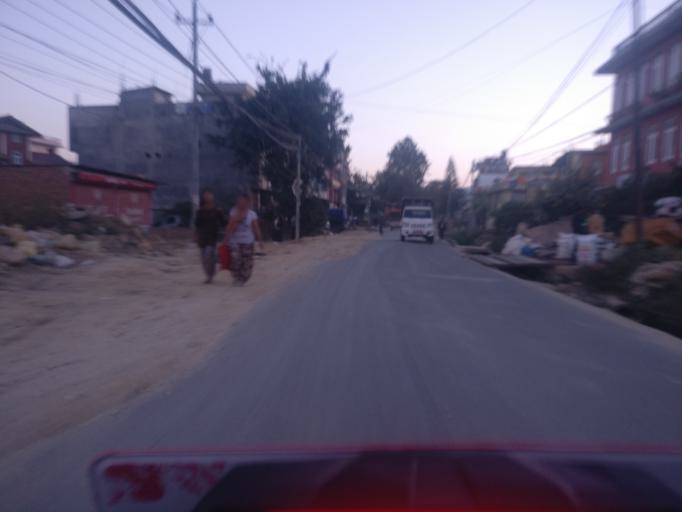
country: NP
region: Central Region
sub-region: Bagmati Zone
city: Patan
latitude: 27.6473
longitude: 85.3199
